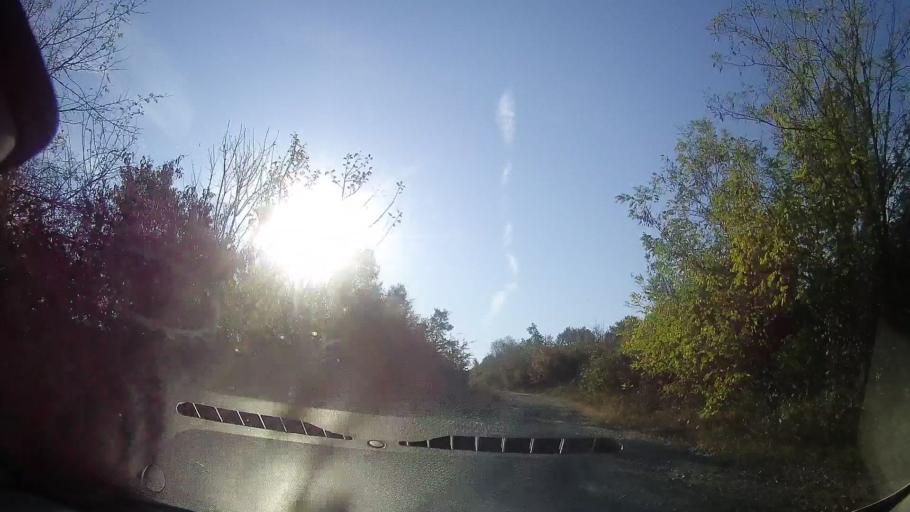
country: RO
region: Timis
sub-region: Comuna Bogda
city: Bogda
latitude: 45.9491
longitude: 21.6183
